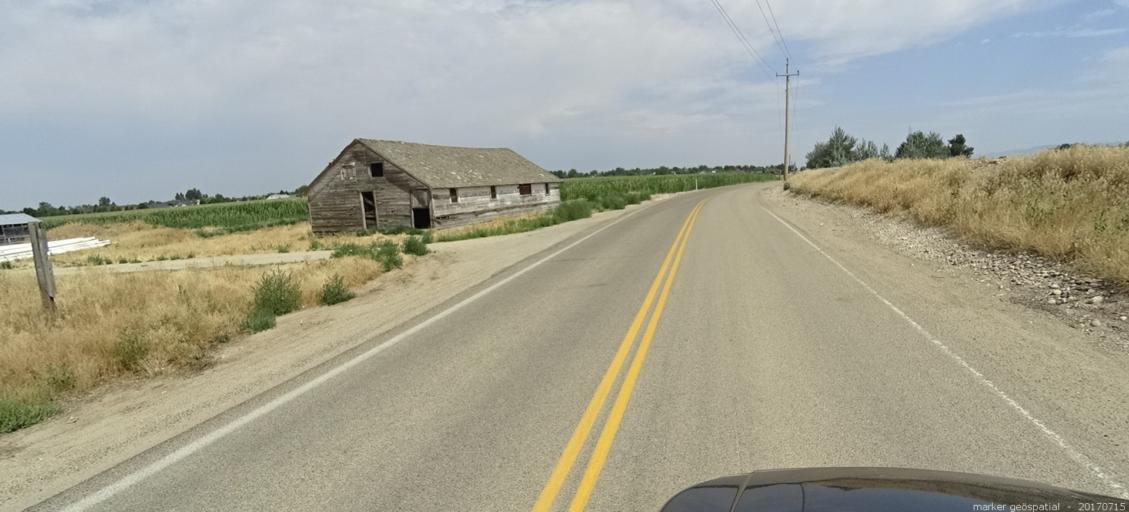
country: US
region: Idaho
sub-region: Ada County
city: Garden City
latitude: 43.5369
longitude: -116.2743
